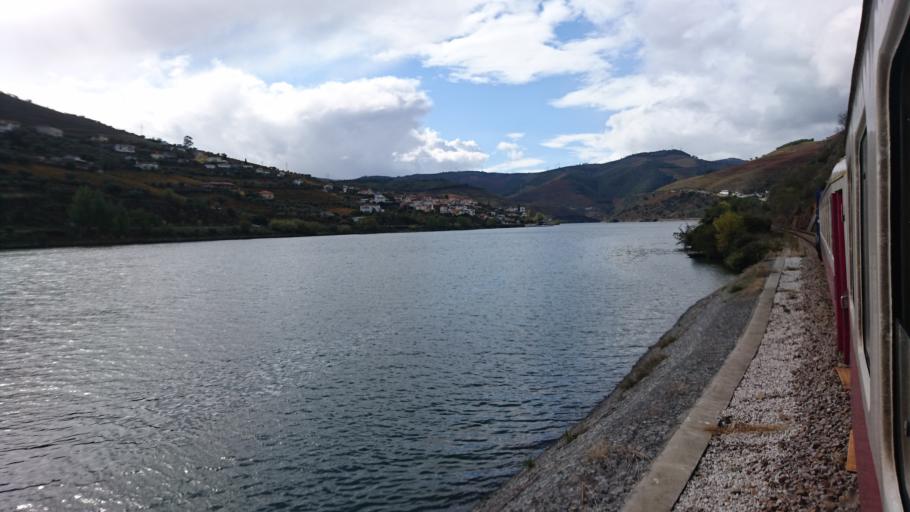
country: PT
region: Viseu
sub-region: Armamar
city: Armamar
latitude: 41.1582
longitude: -7.6749
